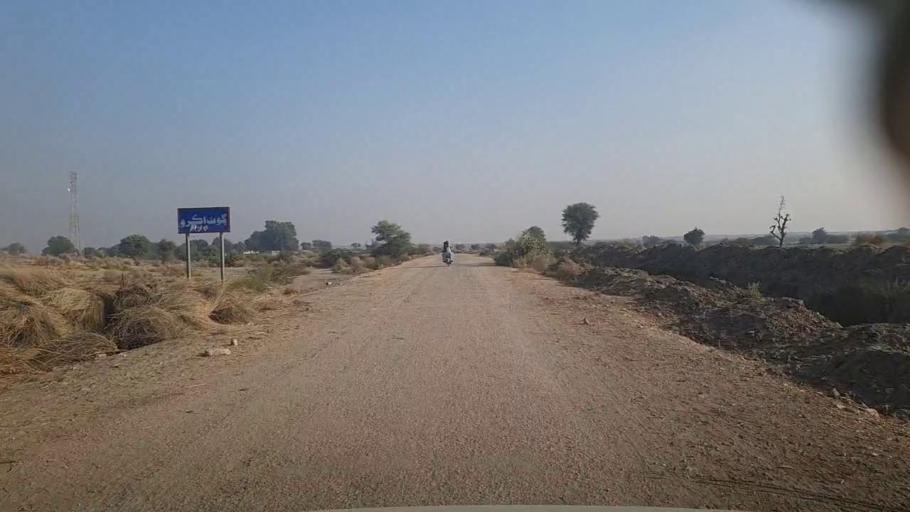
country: PK
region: Sindh
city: Karaundi
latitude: 26.7218
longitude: 68.4922
